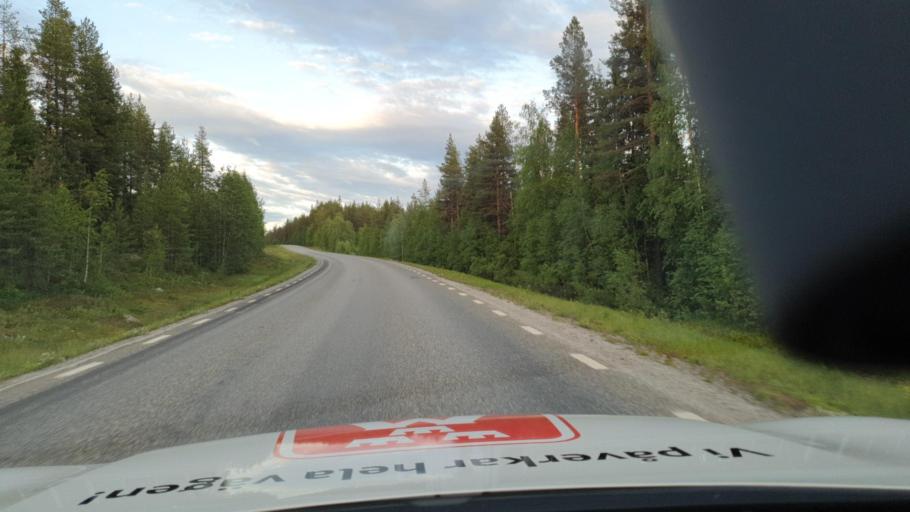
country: SE
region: Vaesterbotten
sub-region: Lycksele Kommun
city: Lycksele
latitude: 64.5839
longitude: 18.6157
